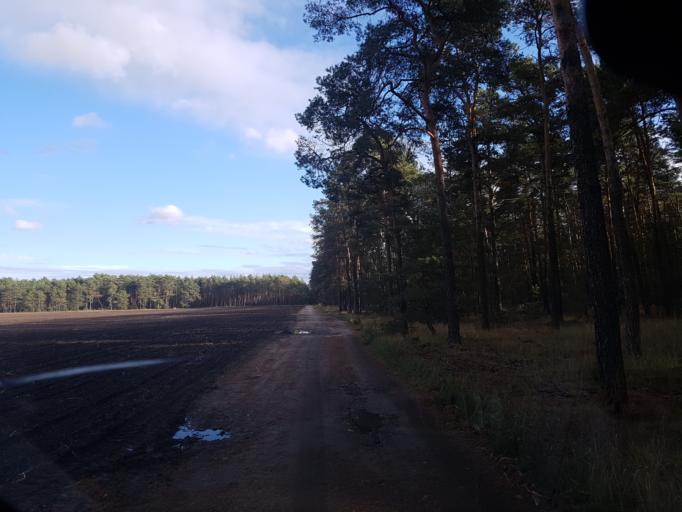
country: DE
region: Brandenburg
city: Finsterwalde
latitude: 51.5575
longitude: 13.6756
